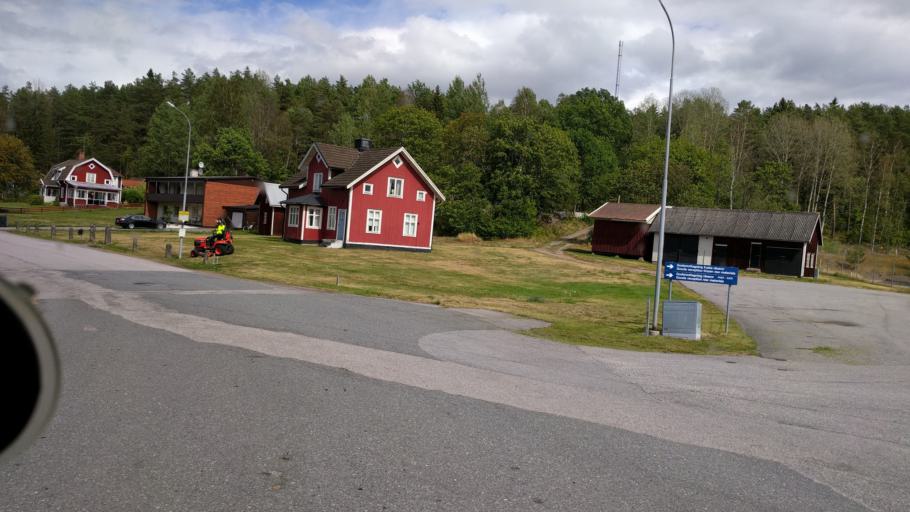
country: SE
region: Kalmar
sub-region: Vimmerby Kommun
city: Vimmerby
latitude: 57.6991
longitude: 16.0037
